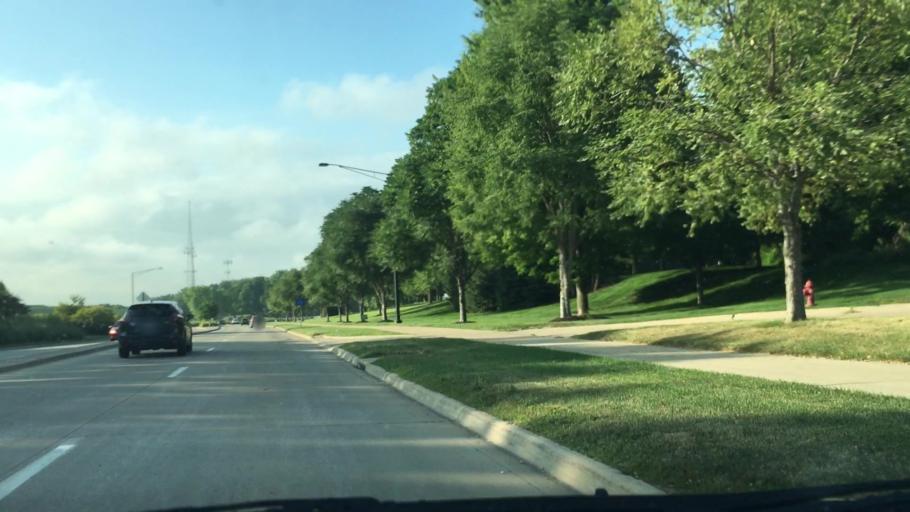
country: US
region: Iowa
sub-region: Johnson County
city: Coralville
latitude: 41.6921
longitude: -91.5665
